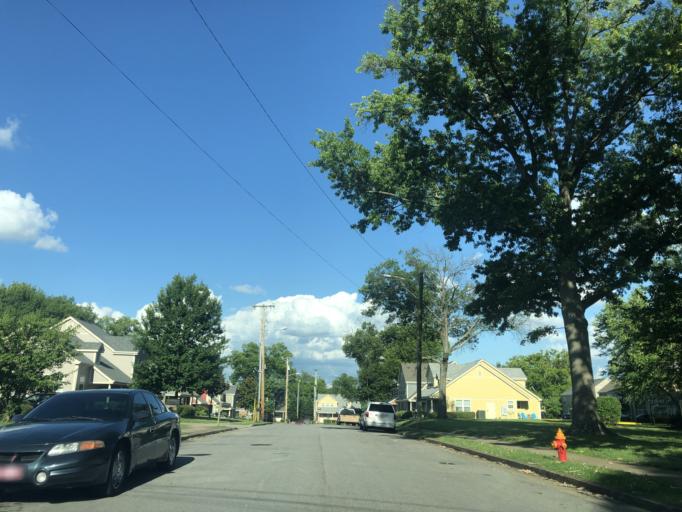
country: US
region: Tennessee
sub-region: Davidson County
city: Nashville
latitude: 36.1796
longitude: -86.7672
